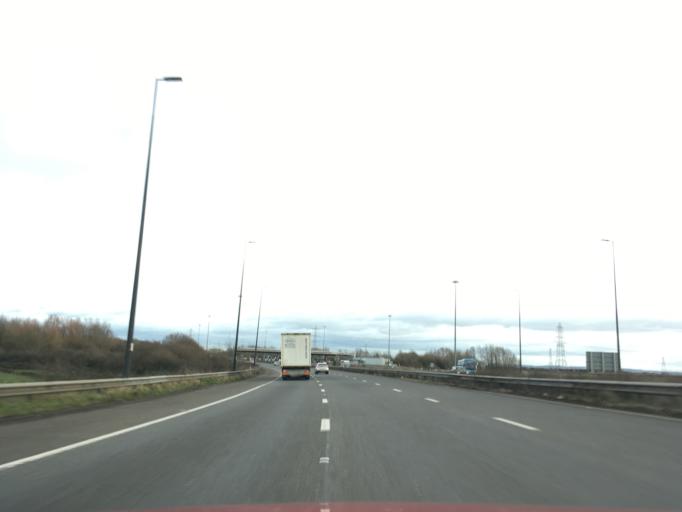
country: GB
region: Wales
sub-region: Monmouthshire
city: Rogiet
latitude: 51.5820
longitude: -2.7918
